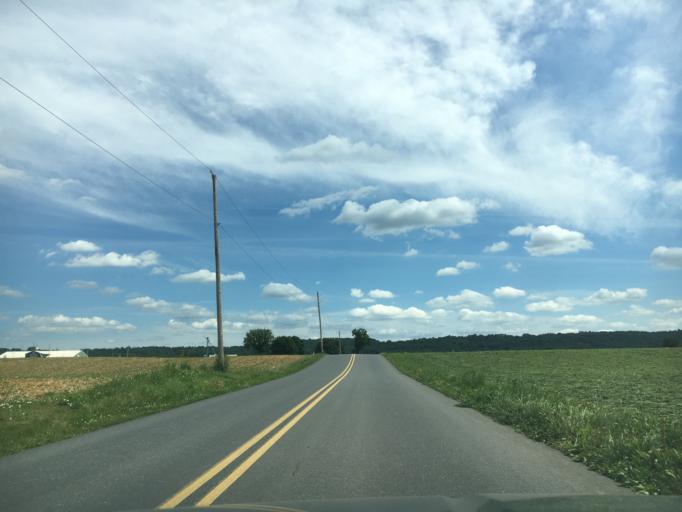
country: US
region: Pennsylvania
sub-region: Berks County
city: Fleetwood
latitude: 40.4790
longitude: -75.7882
